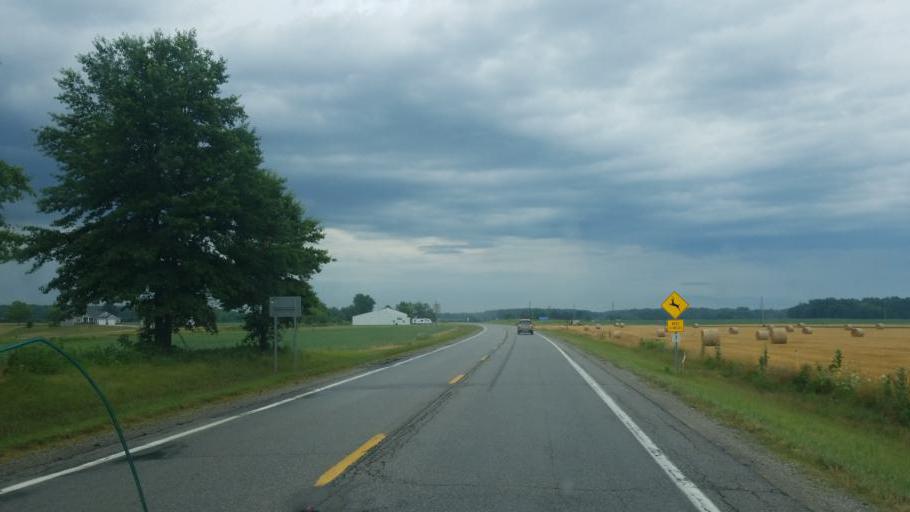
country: US
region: Ohio
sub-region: Williams County
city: Edgerton
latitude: 41.4438
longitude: -84.6738
